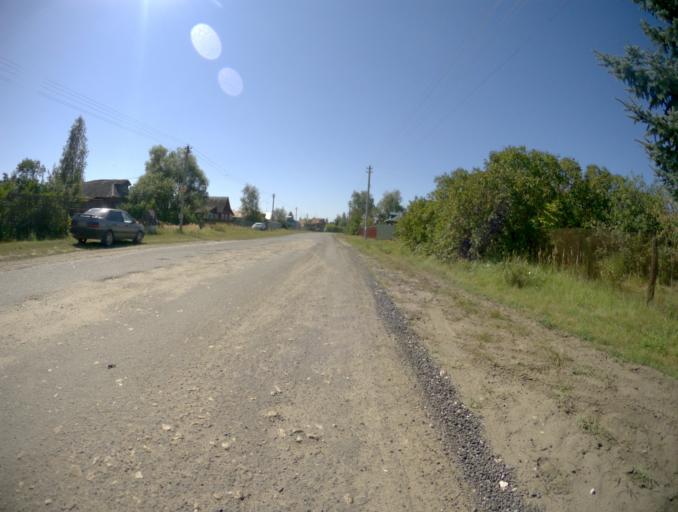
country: RU
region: Vladimir
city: Pokrov
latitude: 55.8640
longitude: 39.2956
